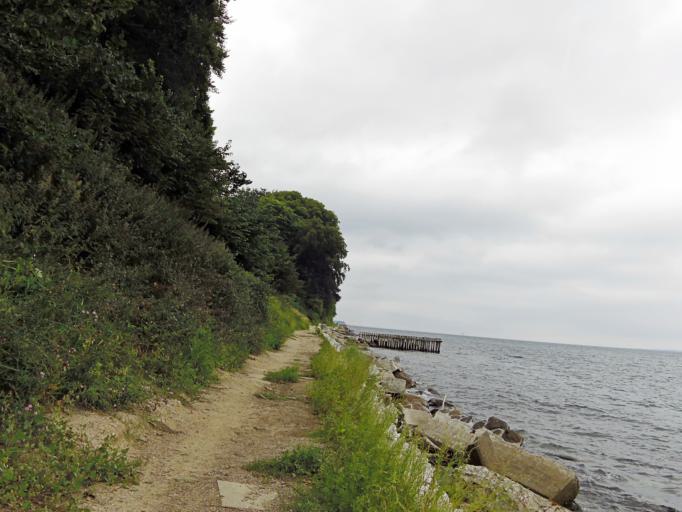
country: DK
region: Capital Region
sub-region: Gentofte Kommune
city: Charlottenlund
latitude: 55.8018
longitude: 12.5880
